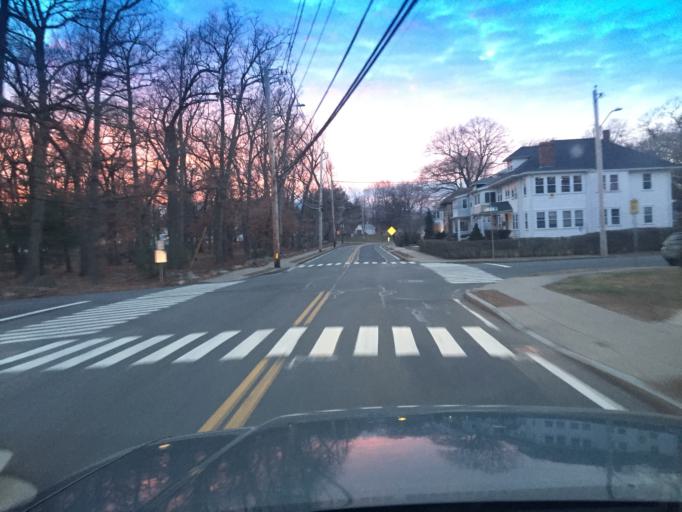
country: US
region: Massachusetts
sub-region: Norfolk County
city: Norwood
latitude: 42.1938
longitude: -71.2102
